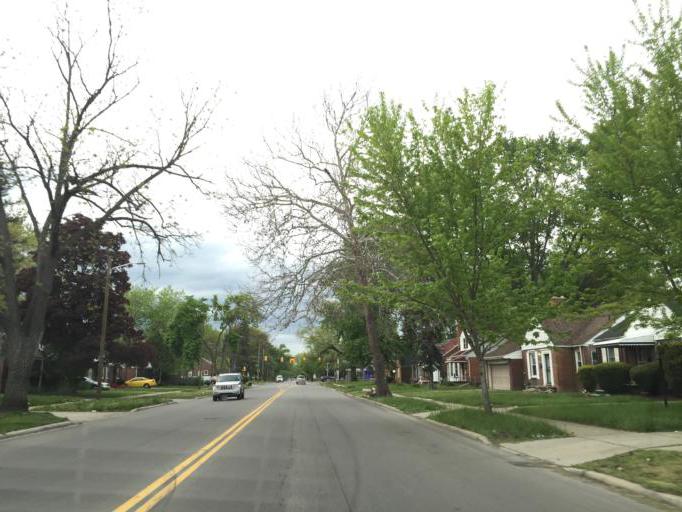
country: US
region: Michigan
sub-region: Wayne County
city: Redford
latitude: 42.3992
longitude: -83.2373
